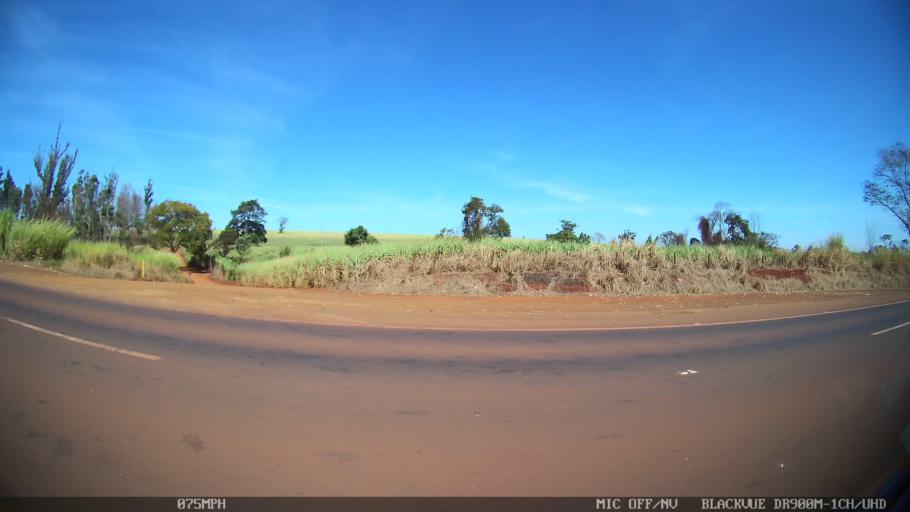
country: BR
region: Sao Paulo
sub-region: Sao Joaquim Da Barra
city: Sao Joaquim da Barra
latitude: -20.5480
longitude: -47.7613
